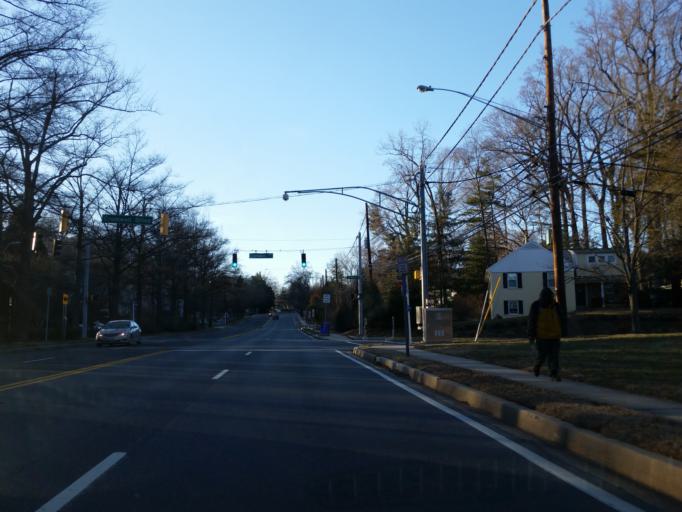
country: US
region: Maryland
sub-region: Montgomery County
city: Brookmont
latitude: 38.9608
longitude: -77.1157
